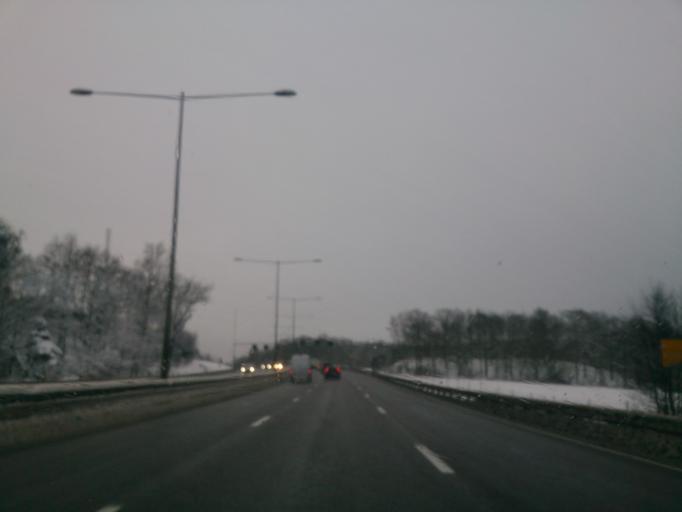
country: SE
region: Stockholm
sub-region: Botkyrka Kommun
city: Eriksberg
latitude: 59.2300
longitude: 17.7990
